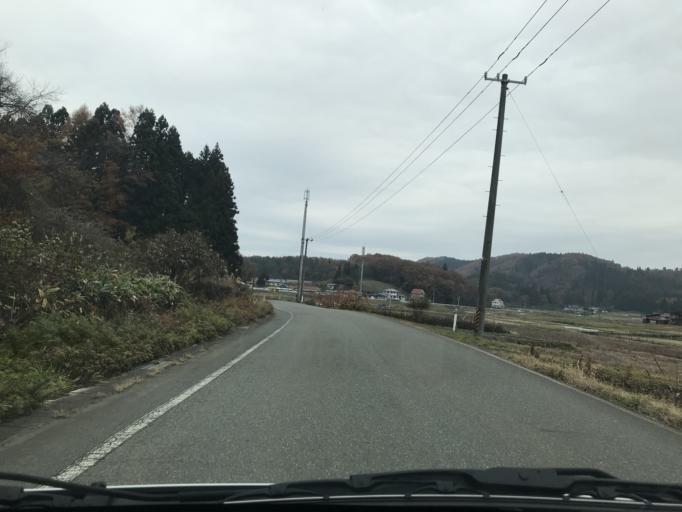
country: JP
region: Iwate
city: Kitakami
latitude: 39.2905
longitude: 141.1745
